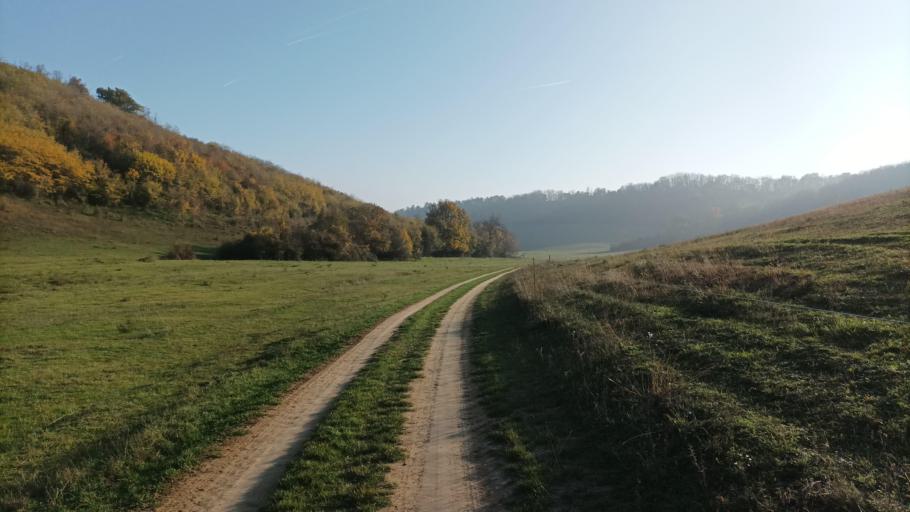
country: HU
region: Tolna
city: Szentgalpuszta
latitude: 46.3306
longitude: 18.6079
